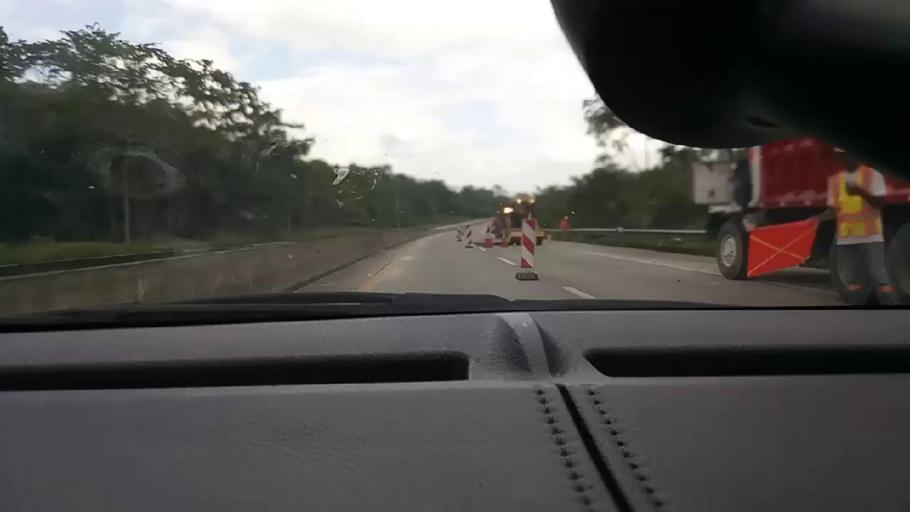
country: PA
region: Panama
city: Chilibre
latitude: 9.1639
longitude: -79.6389
